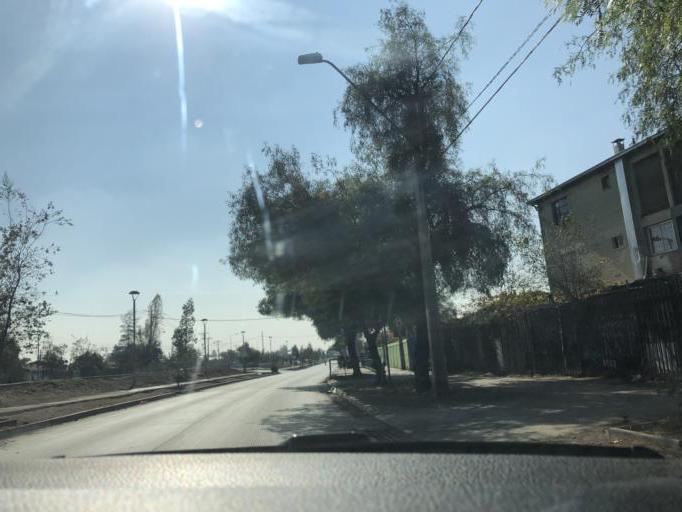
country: CL
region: Santiago Metropolitan
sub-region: Provincia de Santiago
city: La Pintana
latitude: -33.6263
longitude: -70.6283
